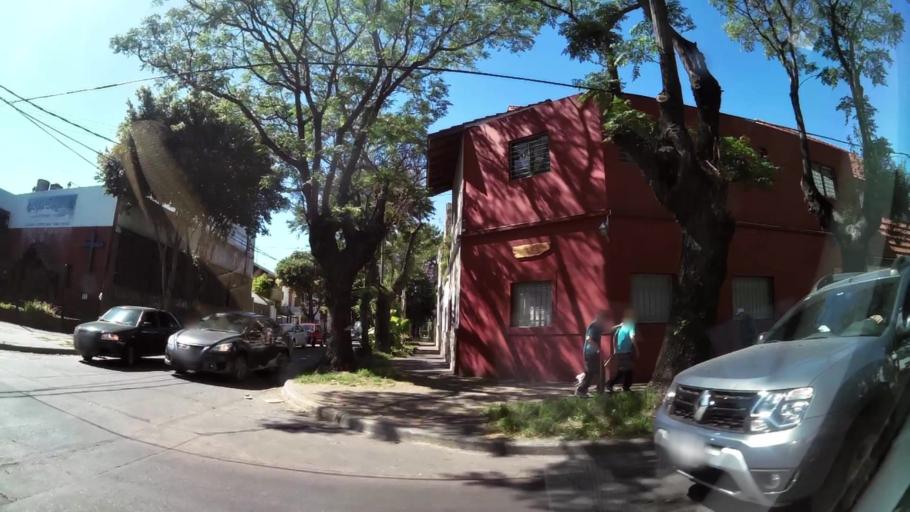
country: AR
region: Buenos Aires
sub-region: Partido de Vicente Lopez
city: Olivos
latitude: -34.5372
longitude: -58.4814
